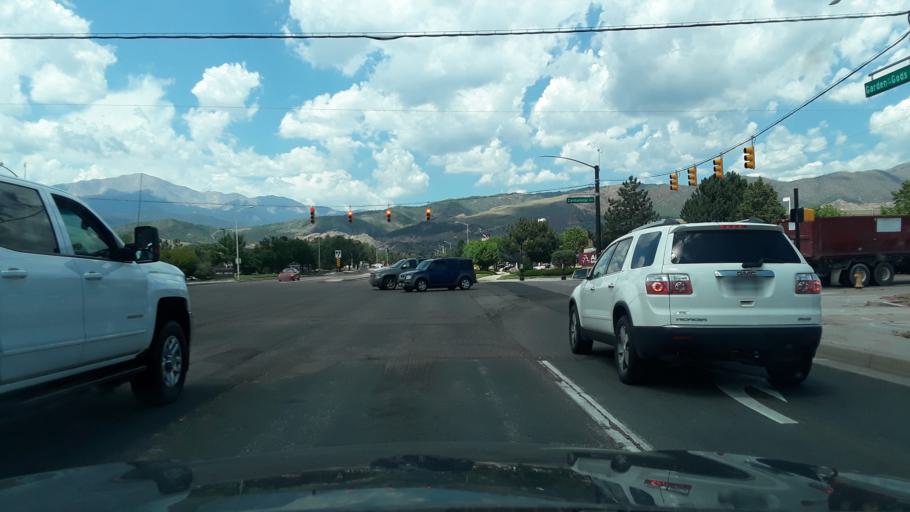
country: US
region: Colorado
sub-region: El Paso County
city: Colorado Springs
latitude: 38.8968
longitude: -104.8509
